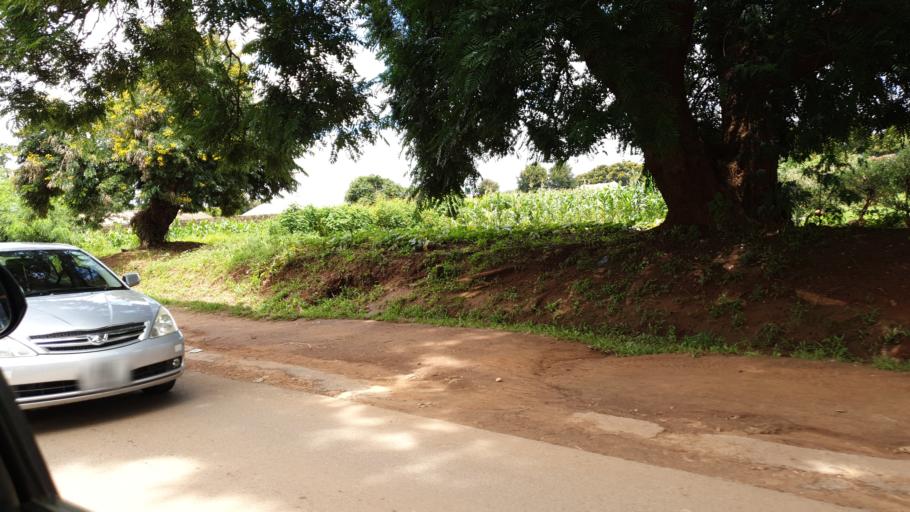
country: ZM
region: Lusaka
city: Lusaka
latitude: -15.4291
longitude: 28.3065
